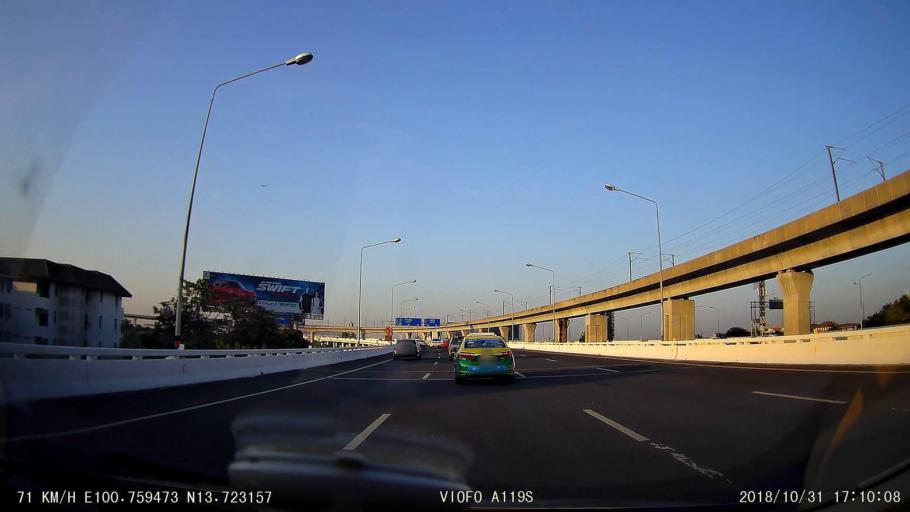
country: TH
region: Bangkok
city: Lat Krabang
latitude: 13.7231
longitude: 100.7595
